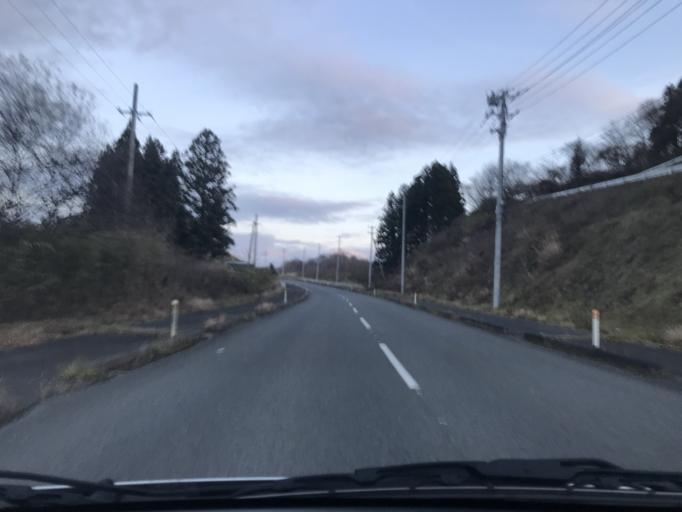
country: JP
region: Iwate
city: Ichinoseki
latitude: 38.8359
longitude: 141.0906
